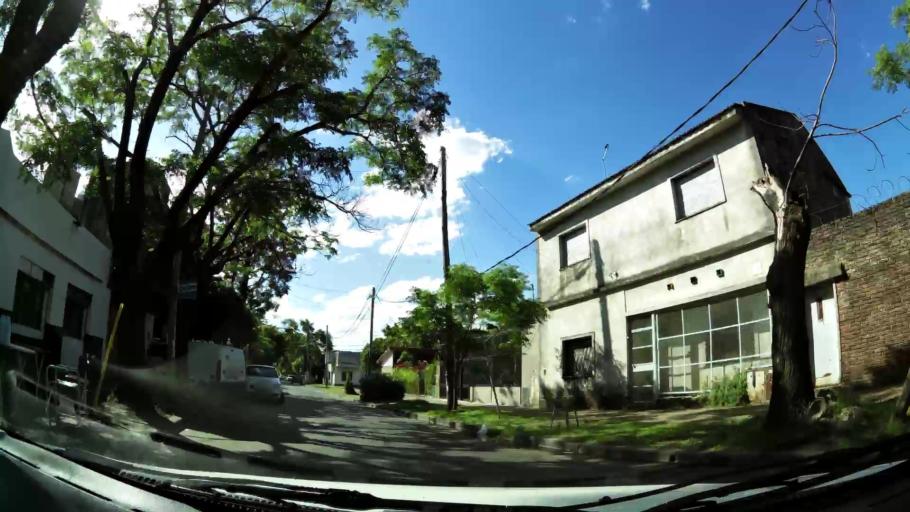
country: AR
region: Buenos Aires
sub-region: Partido de General San Martin
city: General San Martin
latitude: -34.5272
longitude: -58.5745
